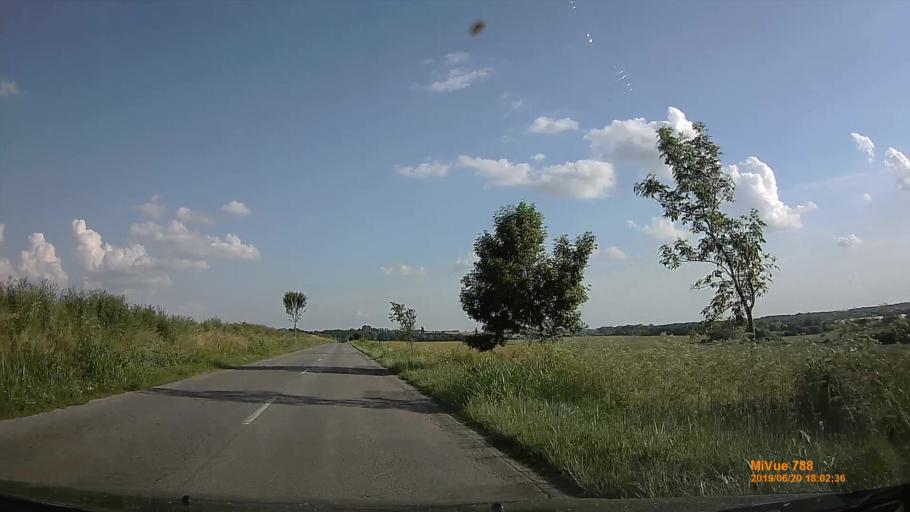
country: HU
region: Baranya
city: Szentlorinc
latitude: 46.0727
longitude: 17.9907
